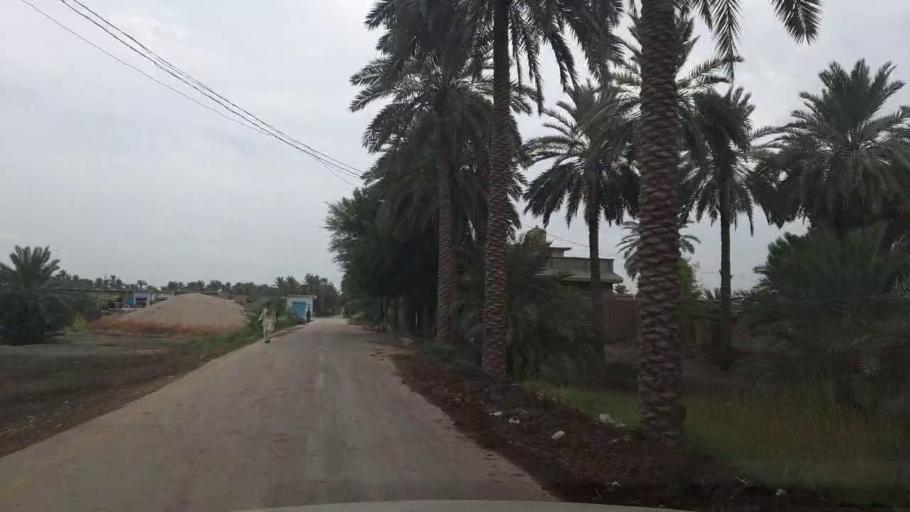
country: PK
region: Sindh
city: Khairpur
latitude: 27.5516
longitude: 68.7509
